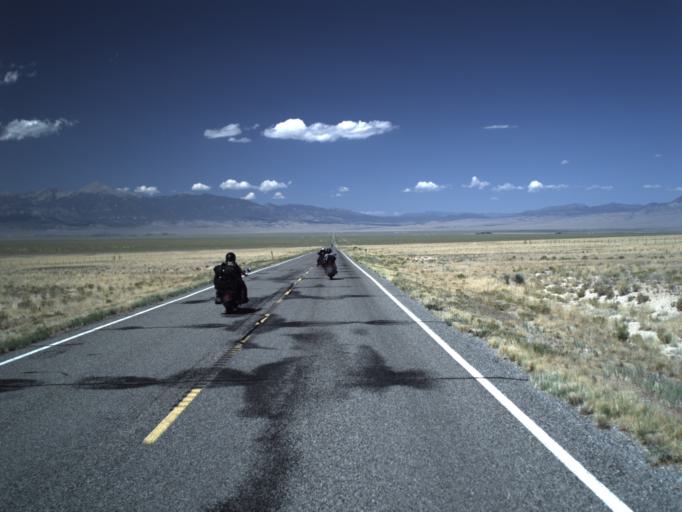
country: US
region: Nevada
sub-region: White Pine County
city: McGill
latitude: 39.0426
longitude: -113.8601
